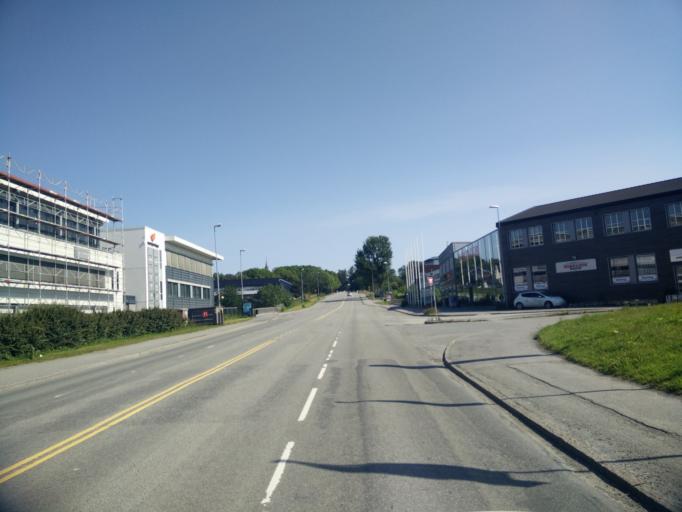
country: NO
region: Sor-Trondelag
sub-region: Trondheim
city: Trondheim
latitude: 63.4432
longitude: 10.4349
